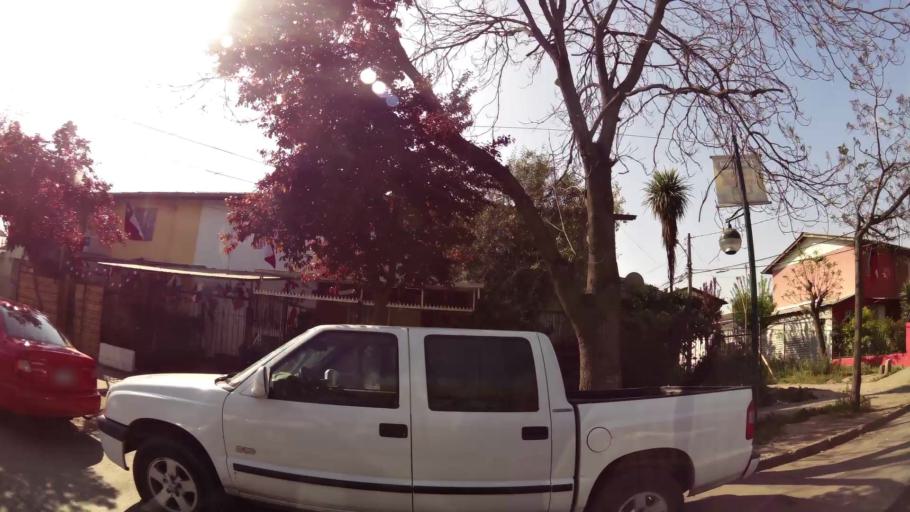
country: CL
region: Santiago Metropolitan
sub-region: Provincia de Santiago
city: Santiago
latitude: -33.4680
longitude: -70.6164
